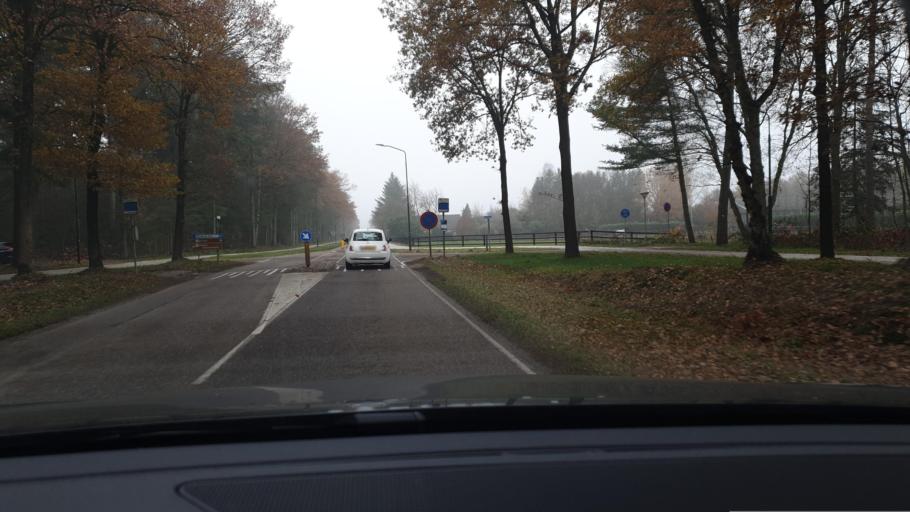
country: NL
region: North Brabant
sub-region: Bergeijk
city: Bergeyk
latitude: 51.3330
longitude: 5.3493
